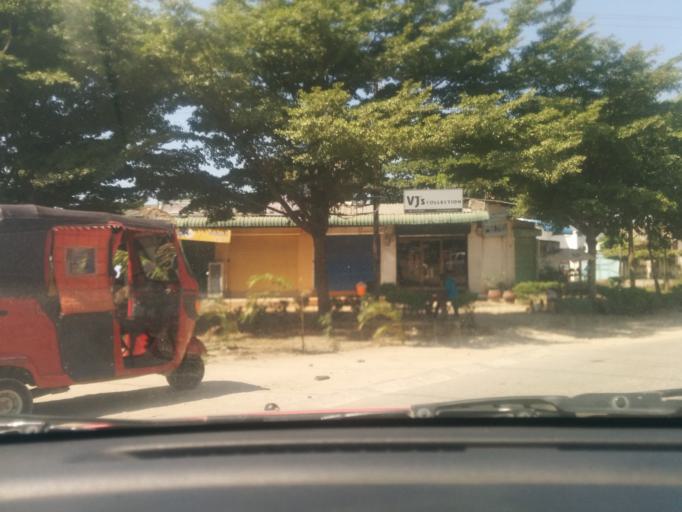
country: TZ
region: Dar es Salaam
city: Magomeni
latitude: -6.7709
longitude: 39.2237
